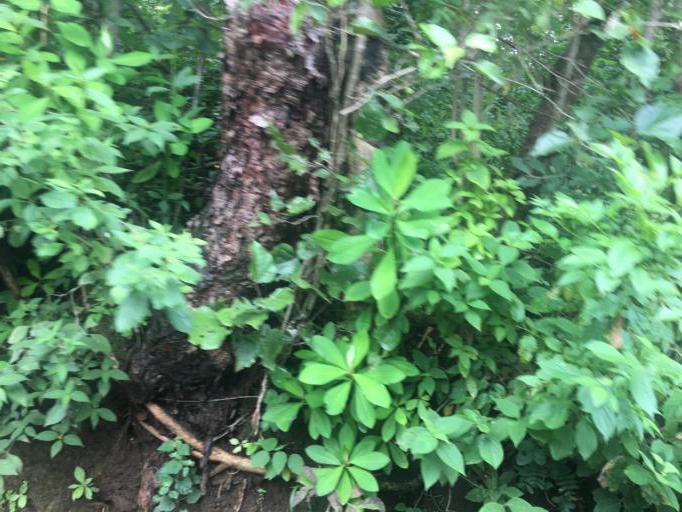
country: GT
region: Escuintla
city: San Vicente Pacaya
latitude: 14.3245
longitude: -90.5619
